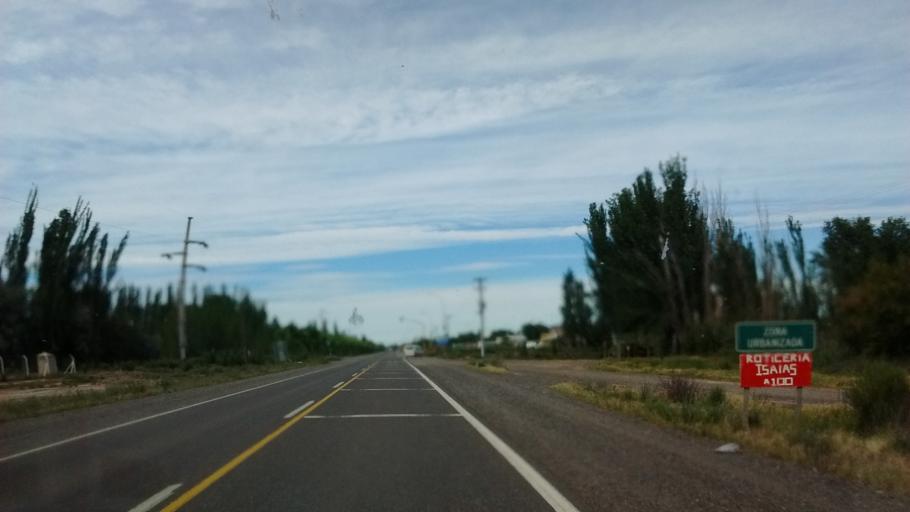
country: AR
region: Rio Negro
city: Contraalmirante Cordero
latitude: -38.6816
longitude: -68.1539
